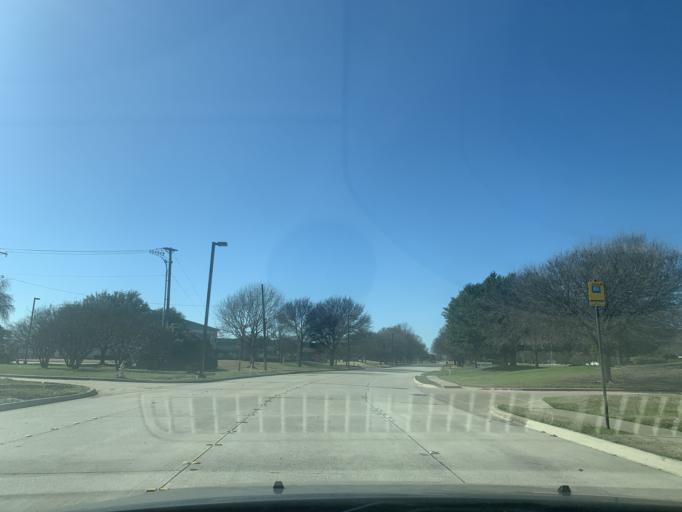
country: US
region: Texas
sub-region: Denton County
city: The Colony
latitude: 33.0687
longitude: -96.8119
